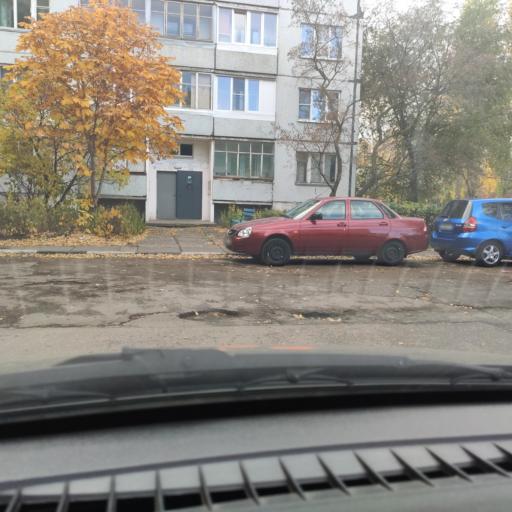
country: RU
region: Samara
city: Tol'yatti
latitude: 53.5302
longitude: 49.3103
